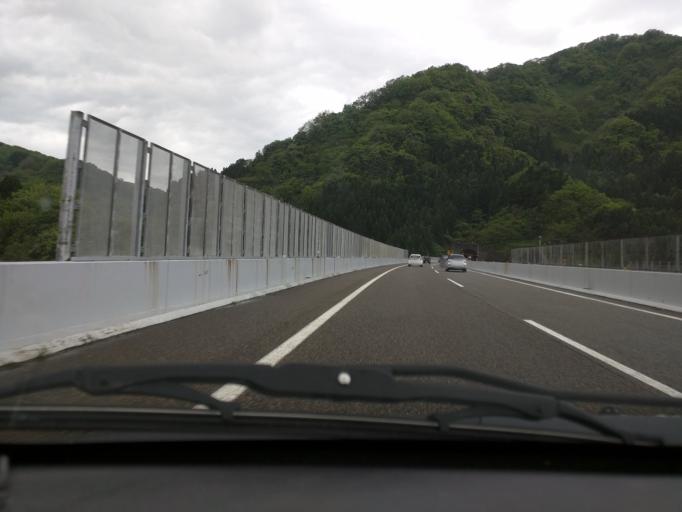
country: JP
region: Niigata
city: Kashiwazaki
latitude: 37.3230
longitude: 138.4585
